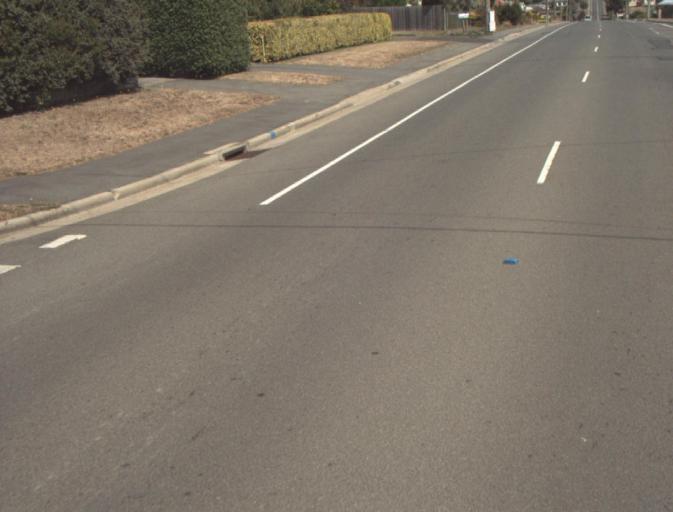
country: AU
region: Tasmania
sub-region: Launceston
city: Newnham
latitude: -41.4100
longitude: 147.1533
